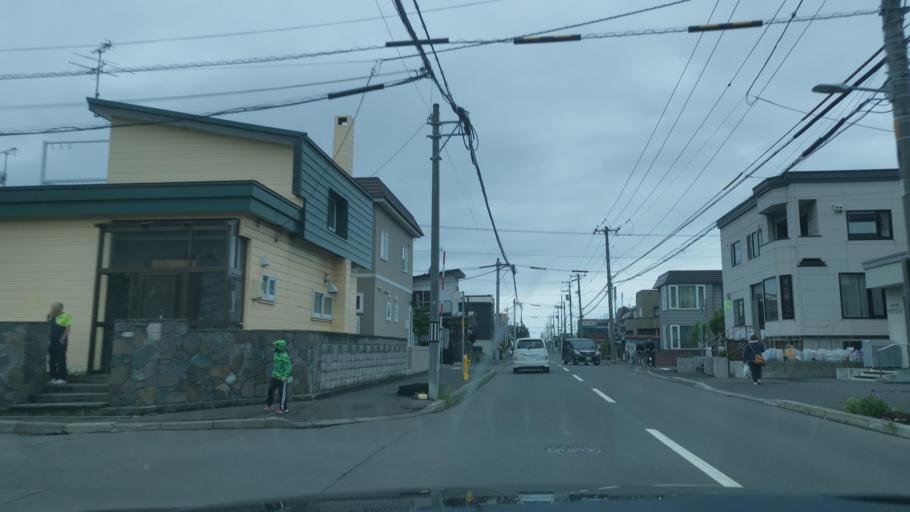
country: JP
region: Hokkaido
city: Sapporo
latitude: 43.1058
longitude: 141.3058
